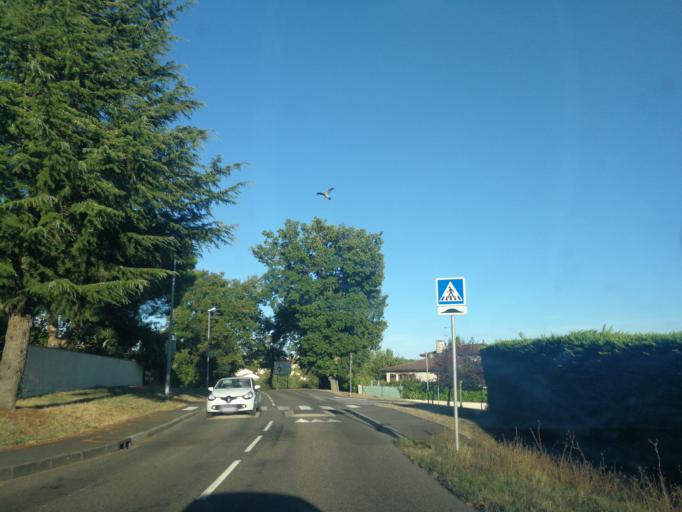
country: FR
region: Midi-Pyrenees
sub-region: Departement de la Haute-Garonne
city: Saint-Jean
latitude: 43.6538
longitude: 1.5086
